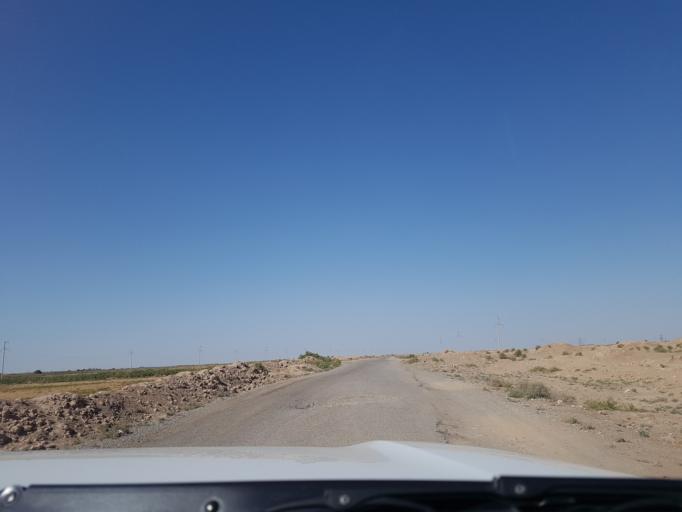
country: IR
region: Razavi Khorasan
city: Sarakhs
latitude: 36.5251
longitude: 61.2419
